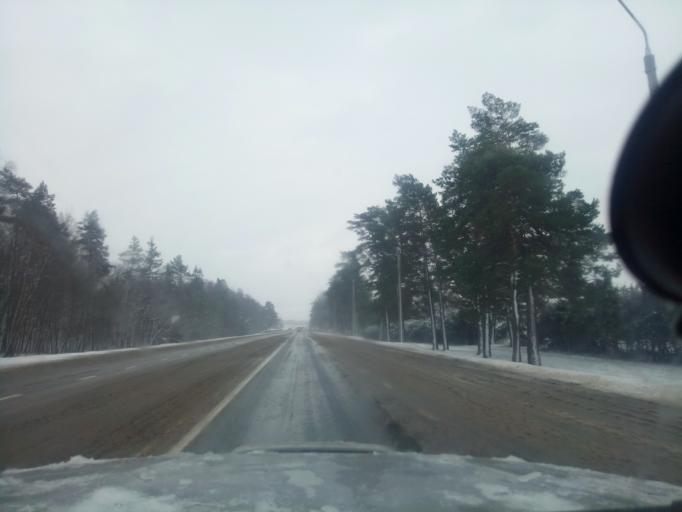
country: BY
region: Minsk
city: Nyasvizh
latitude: 53.2454
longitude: 26.6264
